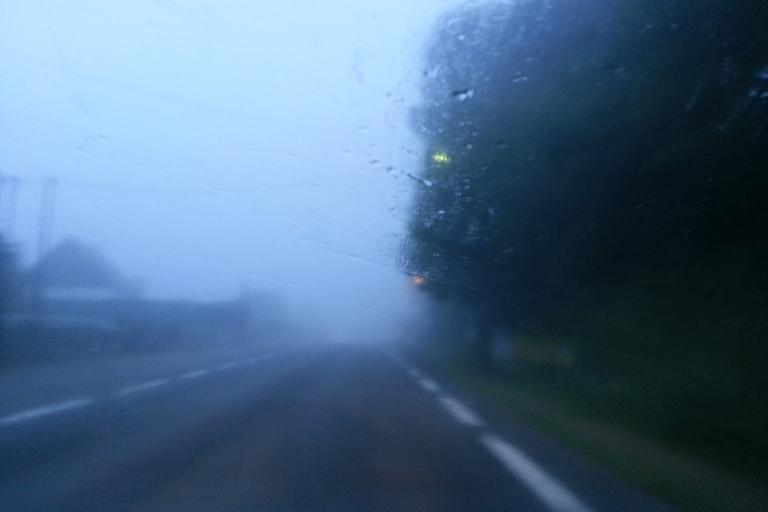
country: FR
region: Brittany
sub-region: Departement du Morbihan
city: Le Faouet
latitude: 48.0451
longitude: -3.4980
